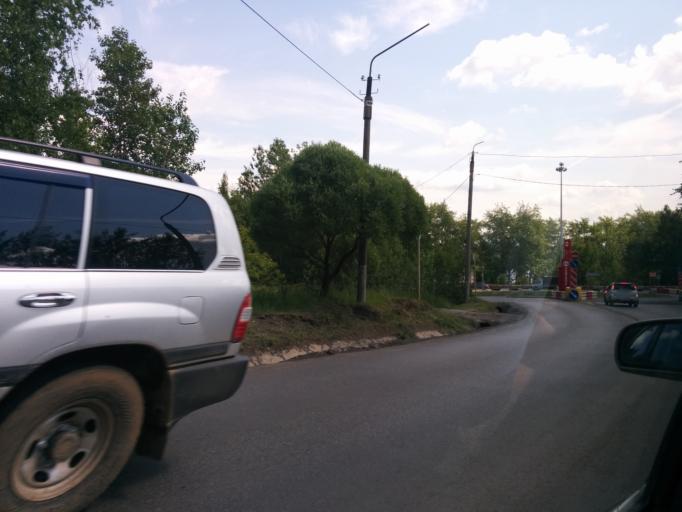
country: RU
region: Perm
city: Perm
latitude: 58.1112
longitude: 56.3219
